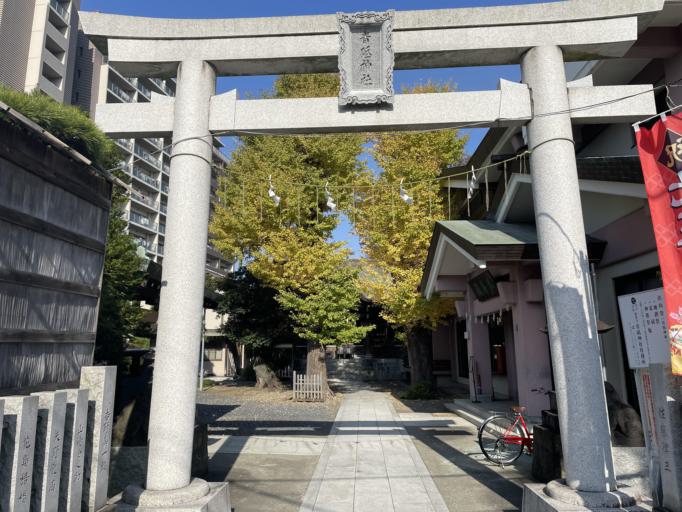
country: JP
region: Chiba
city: Matsudo
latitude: 35.7559
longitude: 139.8565
